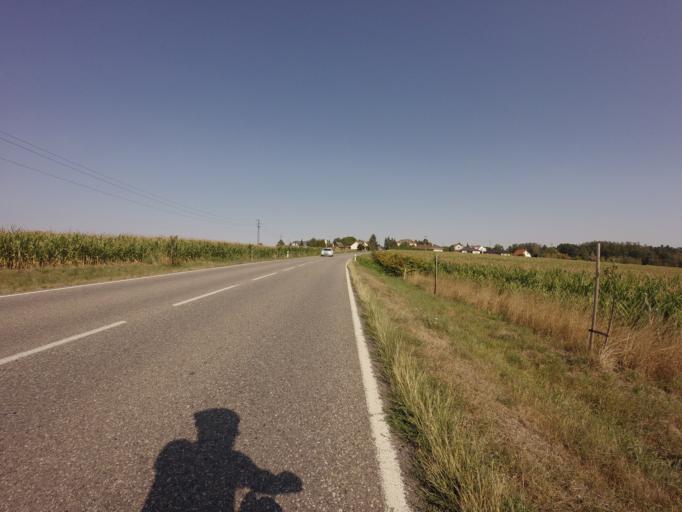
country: CZ
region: Central Bohemia
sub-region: Okres Benesov
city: Benesov
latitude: 49.7978
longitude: 14.6570
